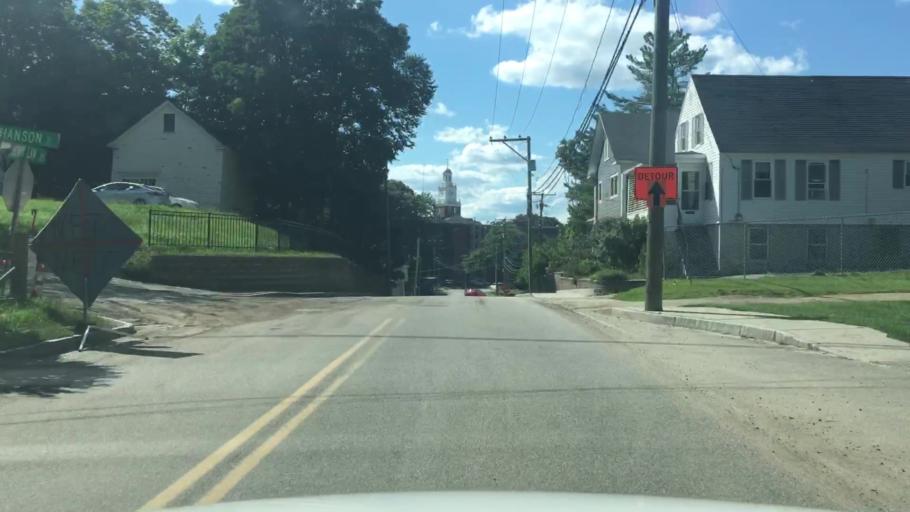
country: US
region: New Hampshire
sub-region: Strafford County
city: Dover
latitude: 43.1927
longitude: -70.8703
